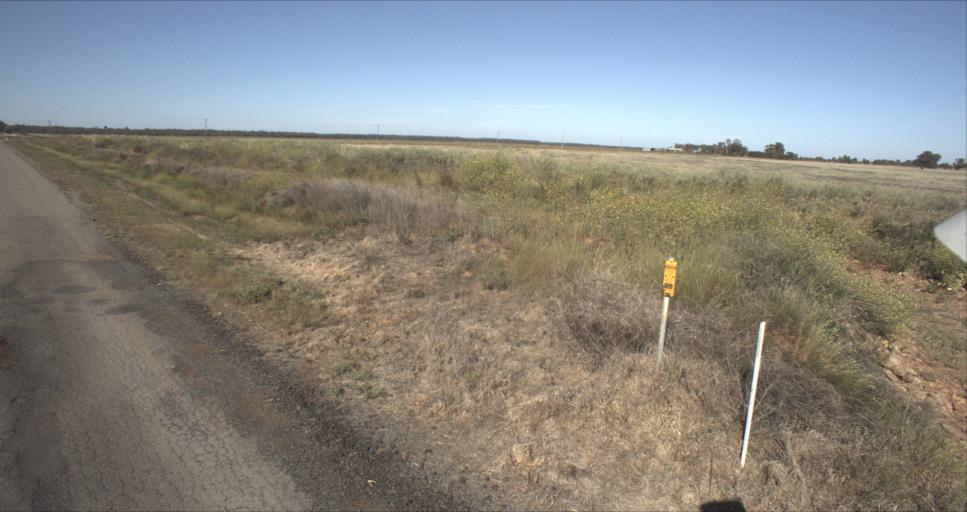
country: AU
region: New South Wales
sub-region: Leeton
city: Leeton
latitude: -34.5815
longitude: 146.3087
